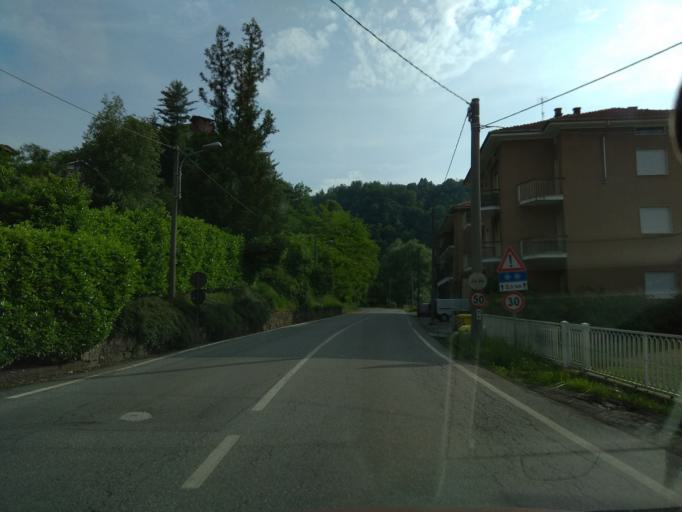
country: IT
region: Piedmont
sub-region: Provincia di Biella
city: Pray
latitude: 45.6713
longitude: 8.2140
